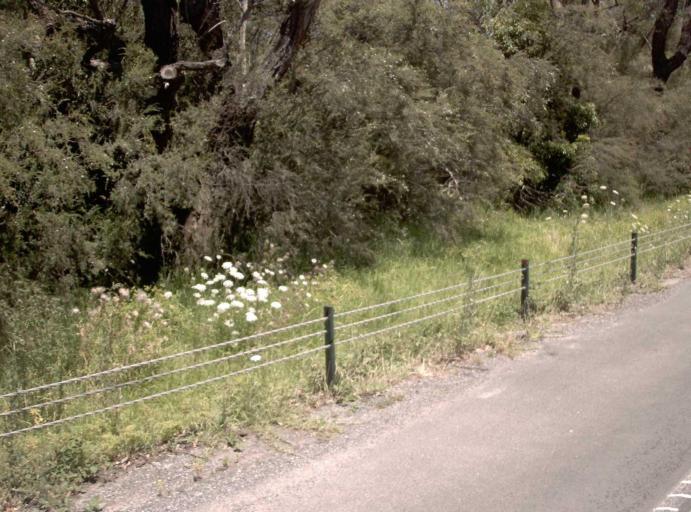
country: AU
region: Victoria
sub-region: Cardinia
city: Garfield
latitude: -38.0688
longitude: 145.6192
